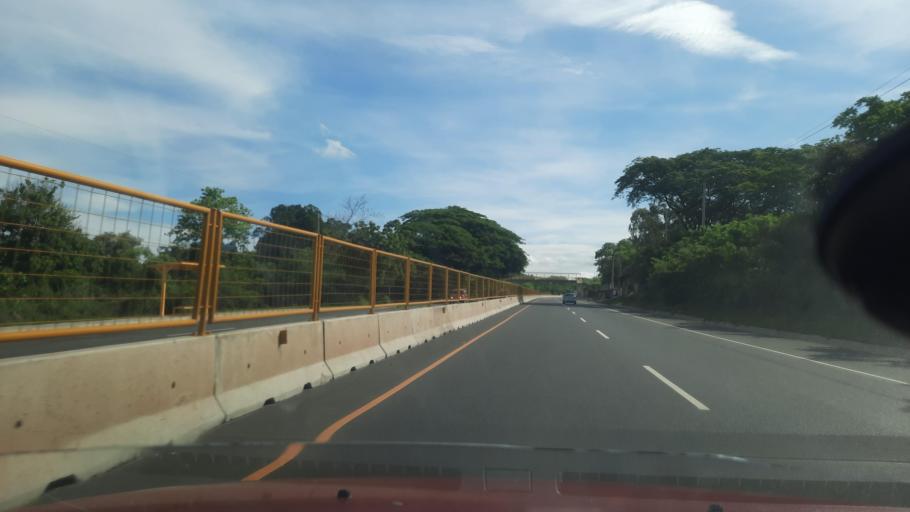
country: SV
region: La Paz
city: El Rosario
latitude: 13.4801
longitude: -88.9990
